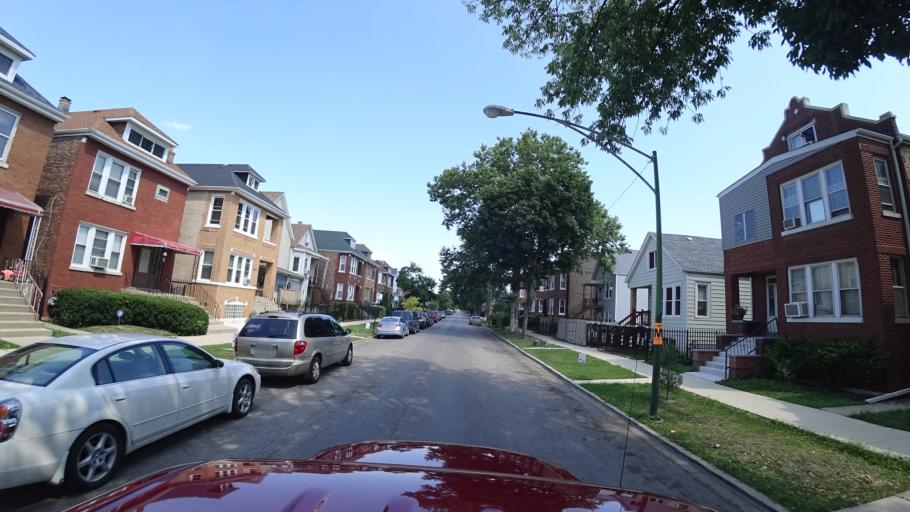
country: US
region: Illinois
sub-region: Cook County
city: Chicago
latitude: 41.8127
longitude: -87.6907
